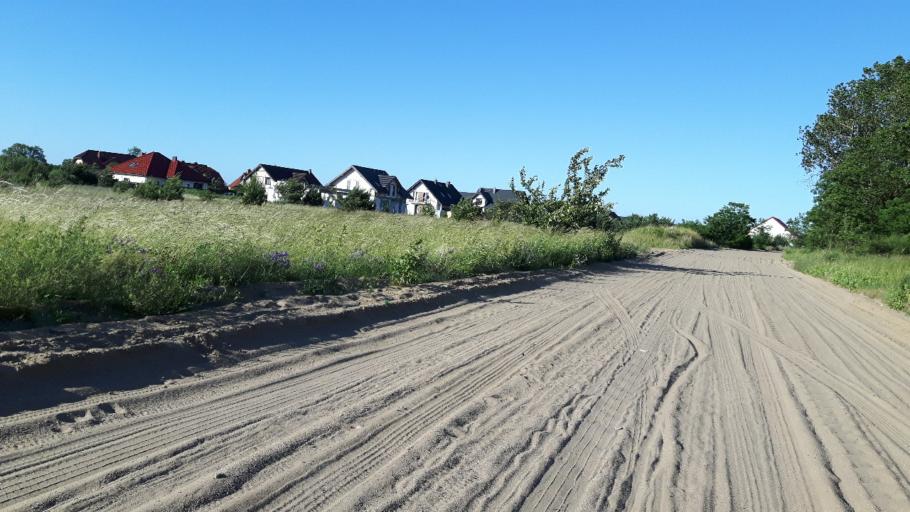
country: PL
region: Pomeranian Voivodeship
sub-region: Powiat pucki
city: Mosty
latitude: 54.6069
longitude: 18.4799
